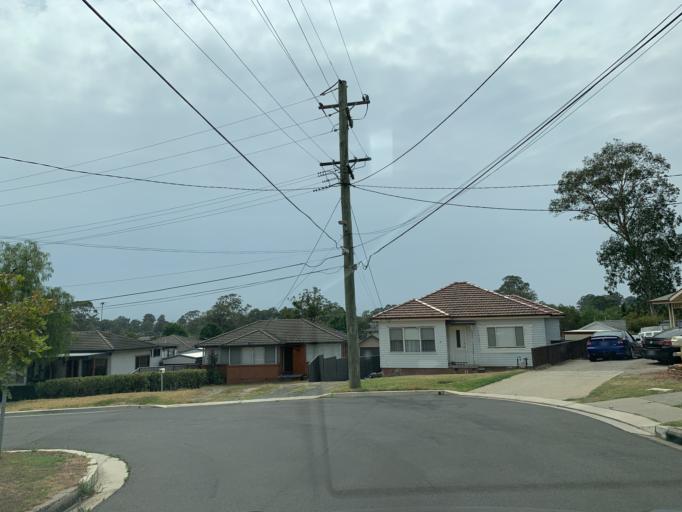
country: AU
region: New South Wales
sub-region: Blacktown
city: Blacktown
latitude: -33.7820
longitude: 150.8966
